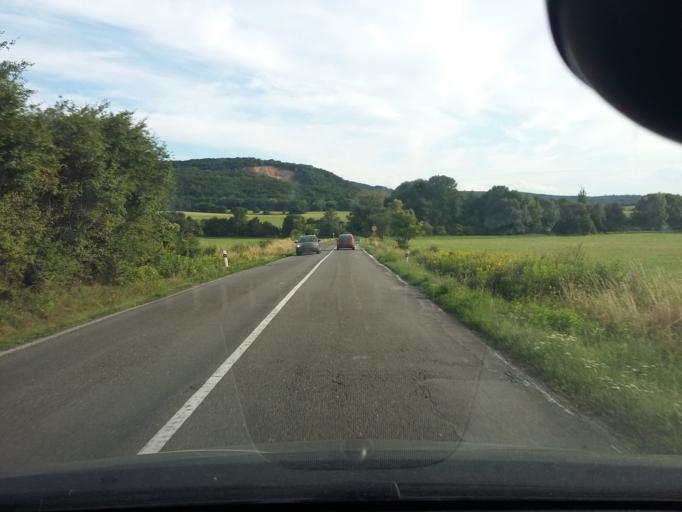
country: SK
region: Bratislavsky
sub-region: Okres Malacky
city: Malacky
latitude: 48.3868
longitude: 17.1548
